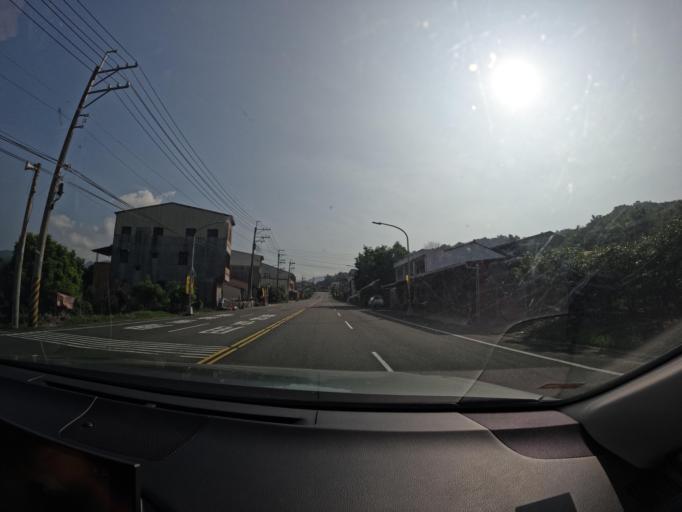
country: TW
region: Taiwan
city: Yujing
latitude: 23.0843
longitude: 120.5242
